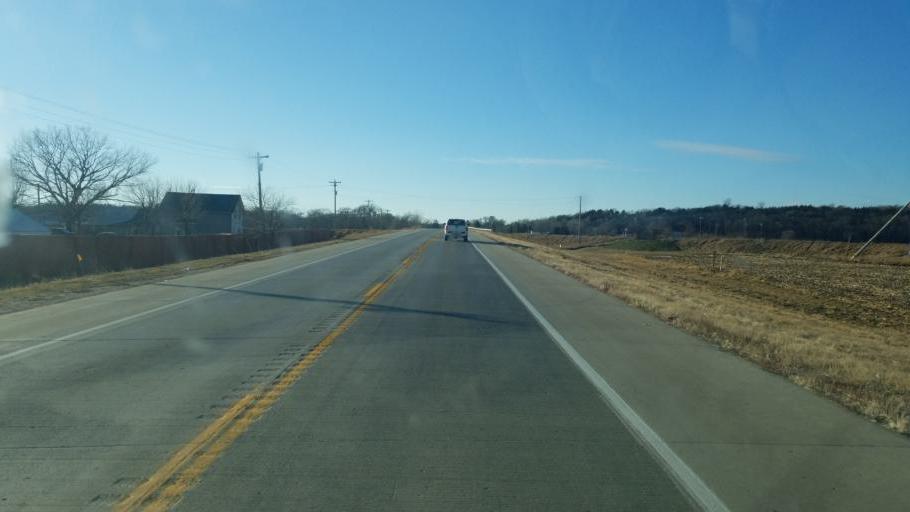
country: US
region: South Dakota
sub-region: Union County
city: Dakota Dunes
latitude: 42.4484
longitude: -96.5543
